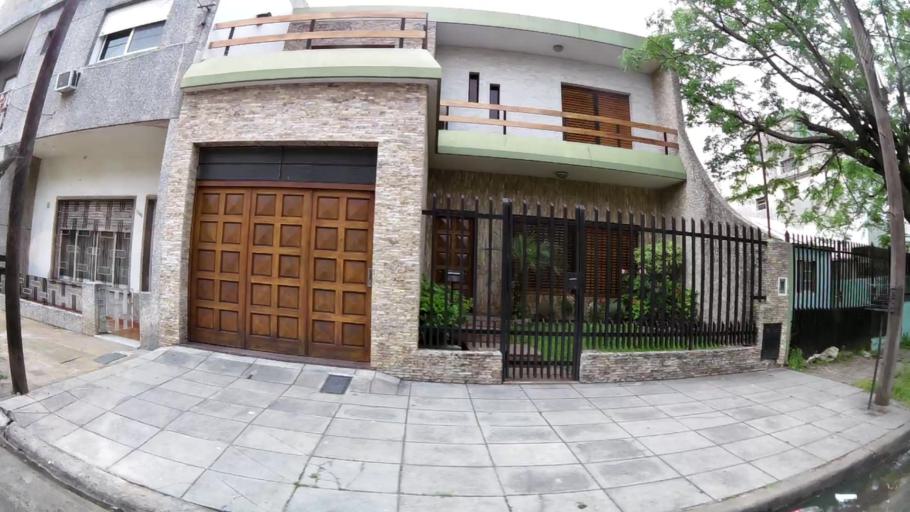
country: AR
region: Buenos Aires F.D.
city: Villa Lugano
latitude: -34.6833
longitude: -58.4981
